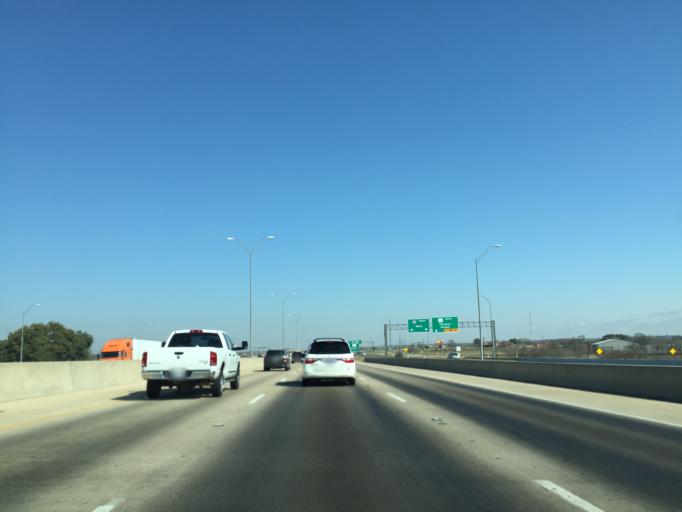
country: US
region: Texas
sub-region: Williamson County
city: Serenada
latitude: 30.6911
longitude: -97.6560
